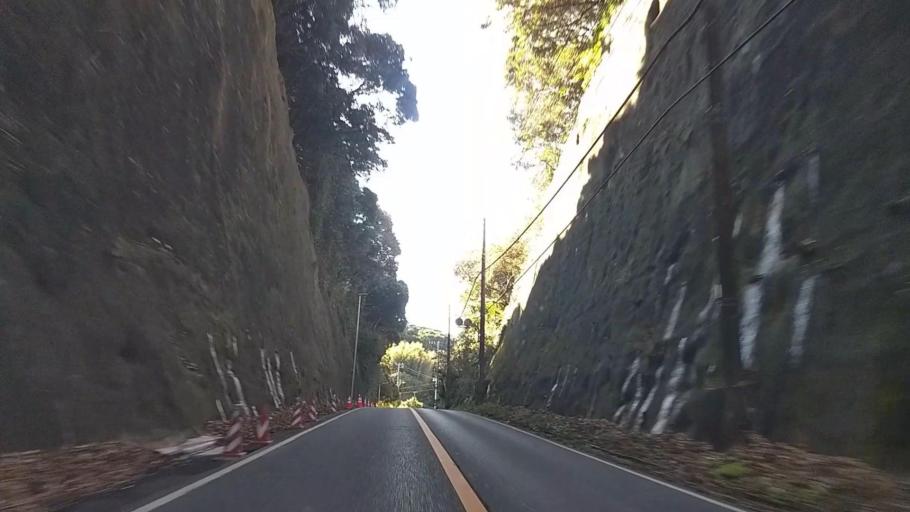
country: JP
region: Chiba
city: Tateyama
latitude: 34.9608
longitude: 139.8547
